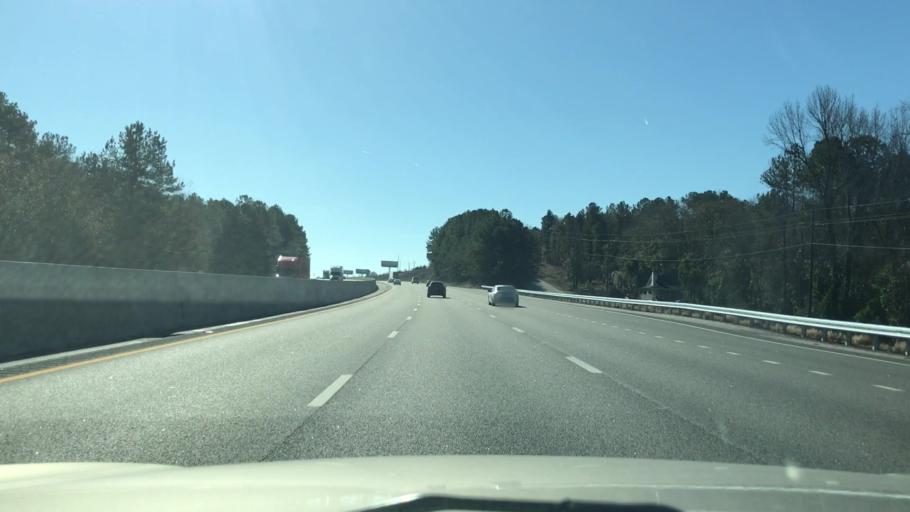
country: US
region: South Carolina
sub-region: Lexington County
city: Pineridge
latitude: 33.8771
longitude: -81.0367
